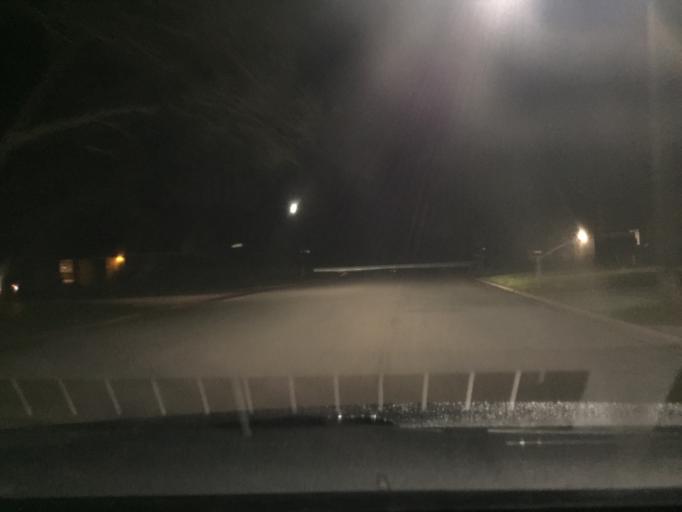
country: US
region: Georgia
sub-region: Chatham County
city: Montgomery
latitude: 32.0017
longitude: -81.1403
